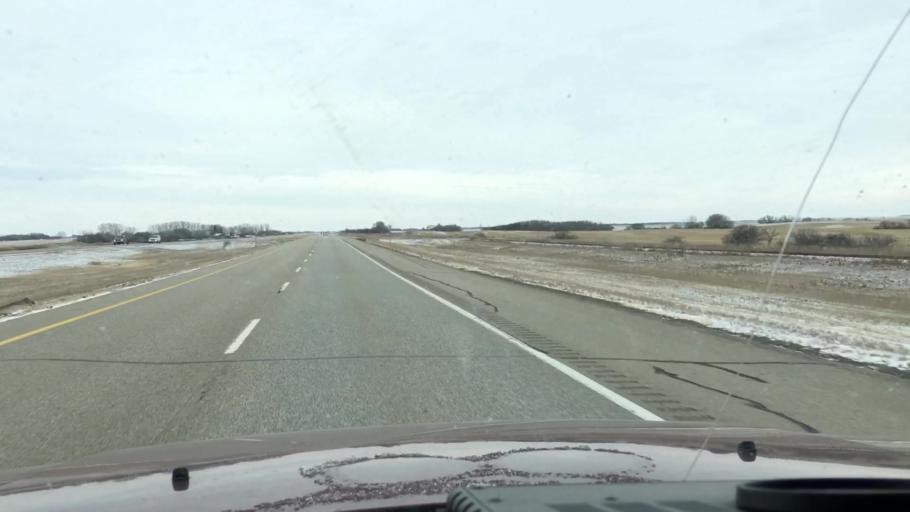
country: CA
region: Saskatchewan
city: Watrous
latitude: 51.3485
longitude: -106.1135
